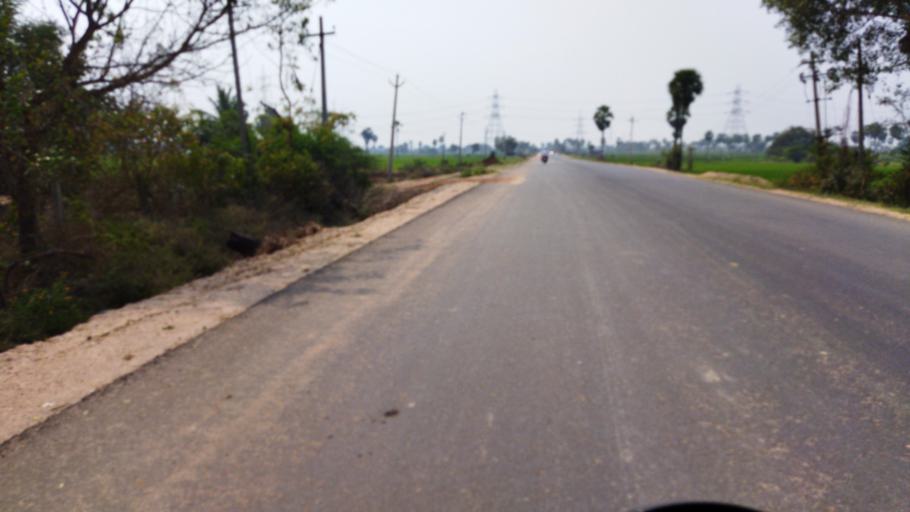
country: IN
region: Telangana
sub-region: Nalgonda
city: Nalgonda
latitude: 17.1329
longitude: 79.3780
